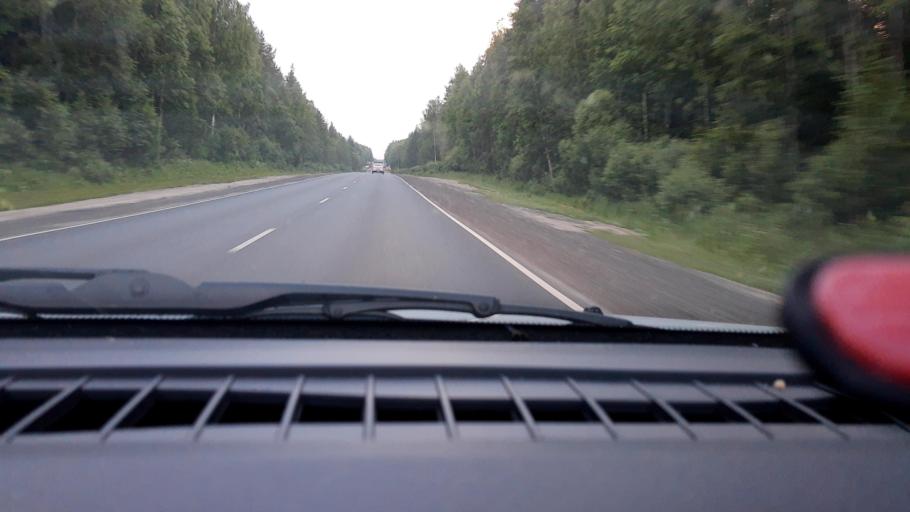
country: RU
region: Nizjnij Novgorod
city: Arzamas
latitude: 55.4242
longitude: 43.9075
